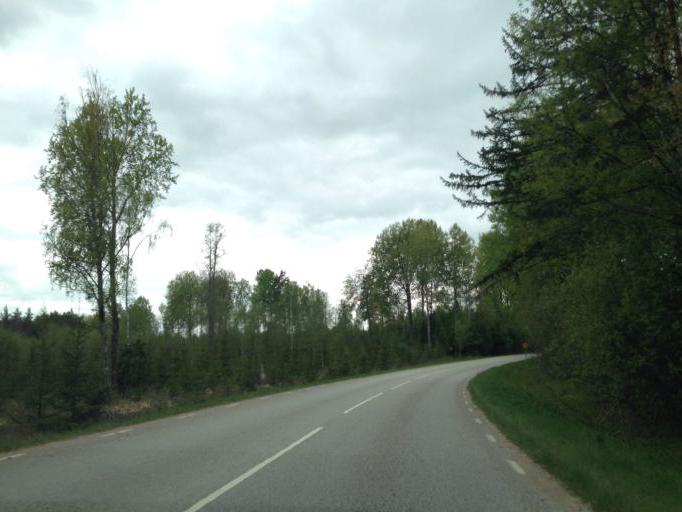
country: SE
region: Soedermanland
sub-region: Eskilstuna Kommun
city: Hallbybrunn
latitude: 59.4042
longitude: 16.3763
